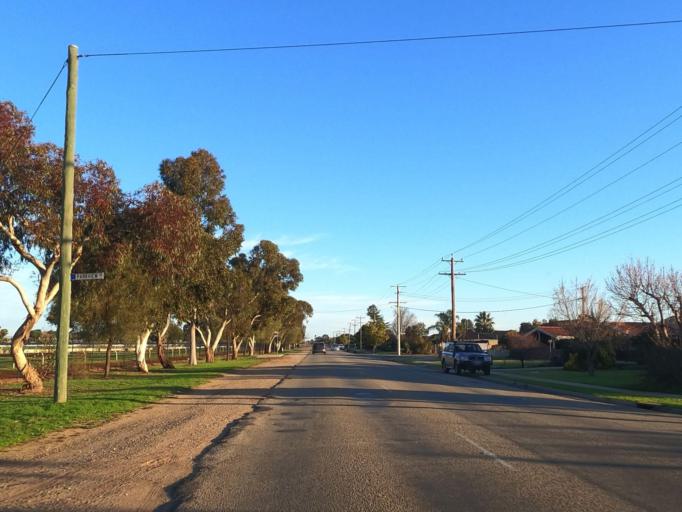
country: AU
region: Victoria
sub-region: Swan Hill
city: Swan Hill
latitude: -35.3501
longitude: 143.5544
